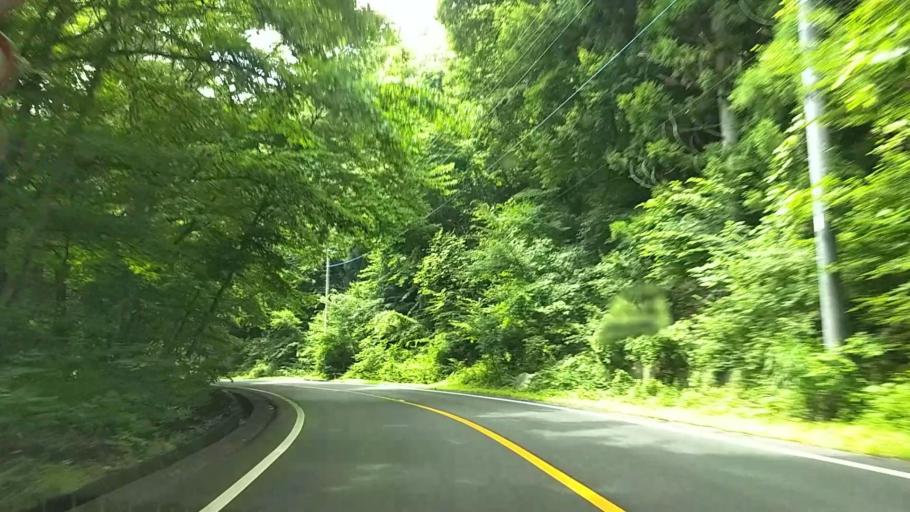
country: JP
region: Yamanashi
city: Fujikawaguchiko
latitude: 35.4772
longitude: 138.5932
